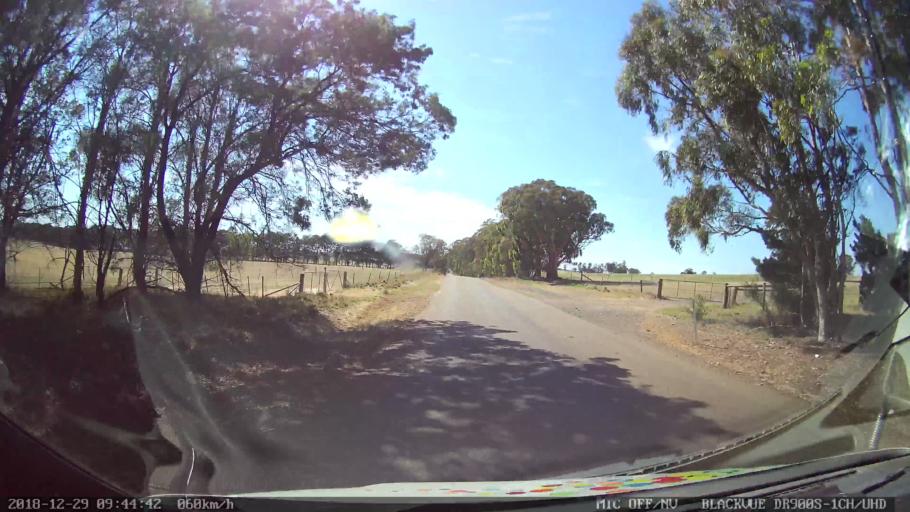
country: AU
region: New South Wales
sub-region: Upper Lachlan Shire
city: Crookwell
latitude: -34.6913
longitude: 149.4278
